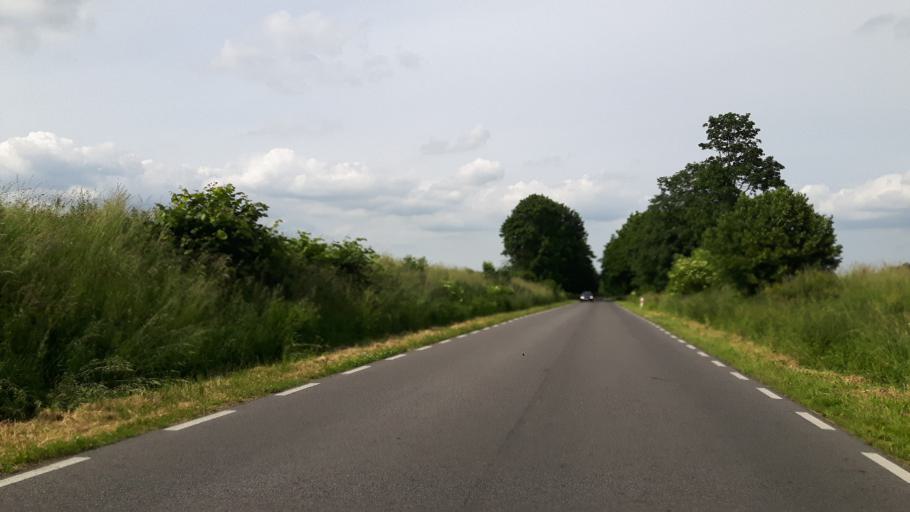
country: PL
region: West Pomeranian Voivodeship
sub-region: Powiat goleniowski
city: Nowogard
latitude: 53.7160
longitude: 15.1193
